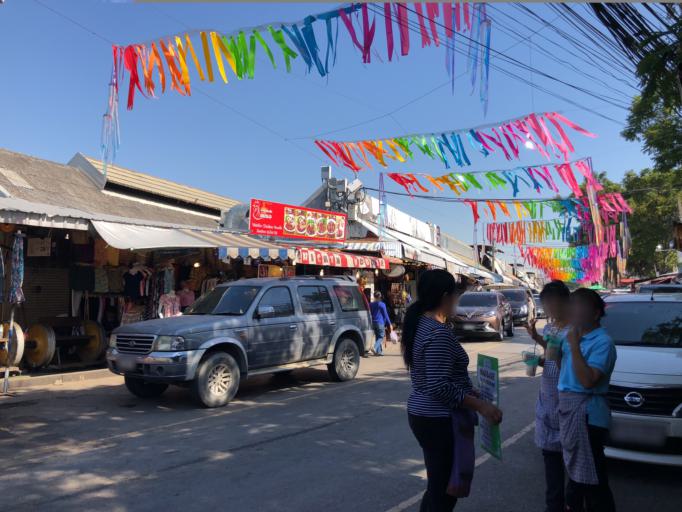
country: TH
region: Bangkok
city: Bang Sue
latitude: 13.7983
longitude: 100.5506
